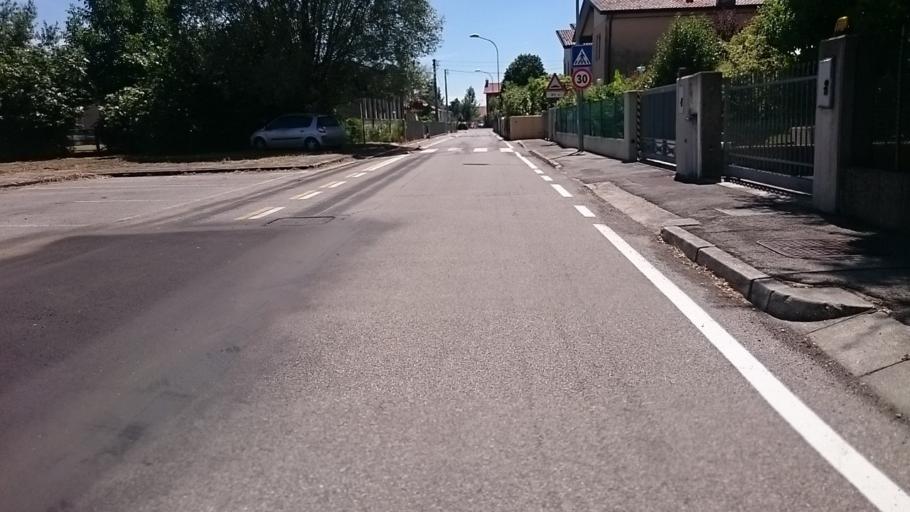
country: IT
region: Veneto
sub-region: Provincia di Padova
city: Villanova
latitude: 45.4906
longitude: 11.9742
